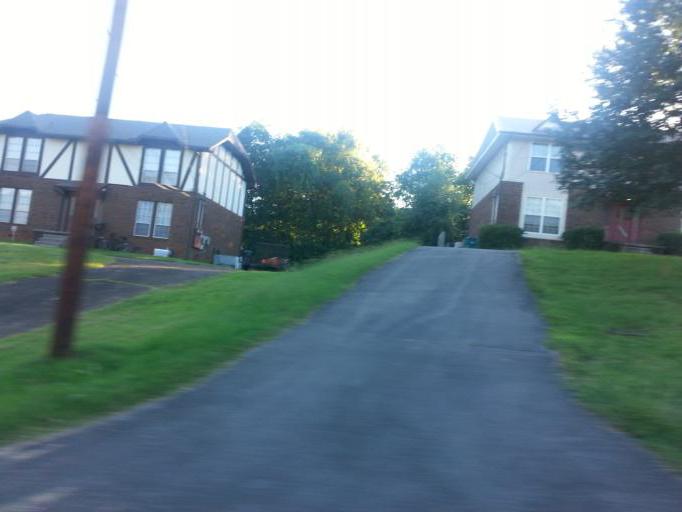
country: US
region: Tennessee
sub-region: Knox County
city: Farragut
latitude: 35.9388
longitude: -84.0818
